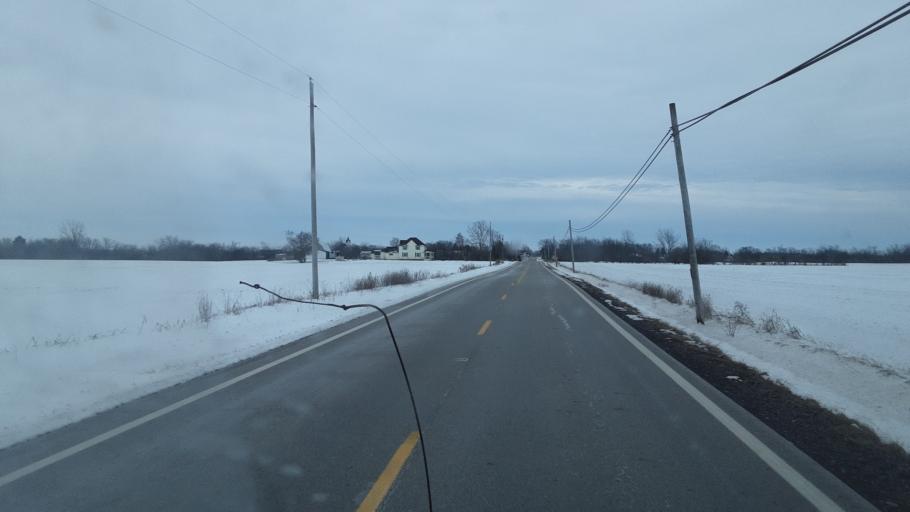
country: US
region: Ohio
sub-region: Madison County
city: Mount Sterling
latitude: 39.6768
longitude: -83.1889
